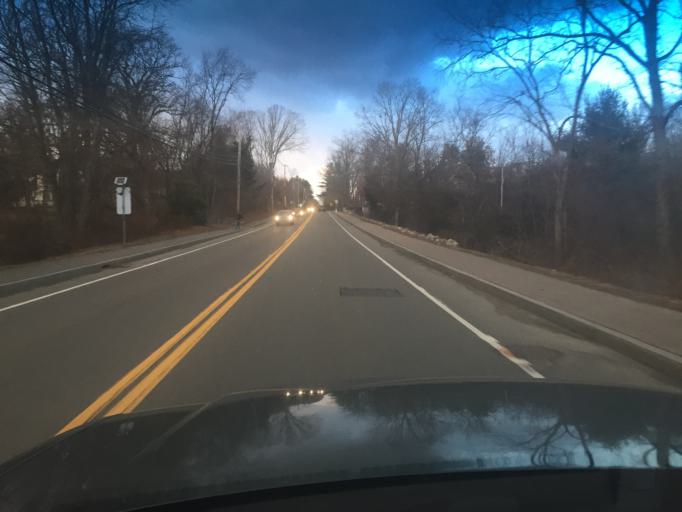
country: US
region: Massachusetts
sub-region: Middlesex County
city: Holliston
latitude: 42.1565
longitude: -71.4434
